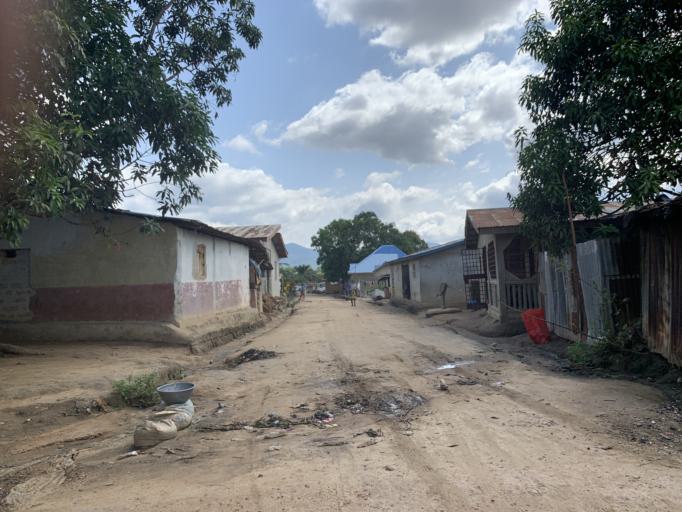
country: SL
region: Western Area
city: Waterloo
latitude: 8.3351
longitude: -13.0515
